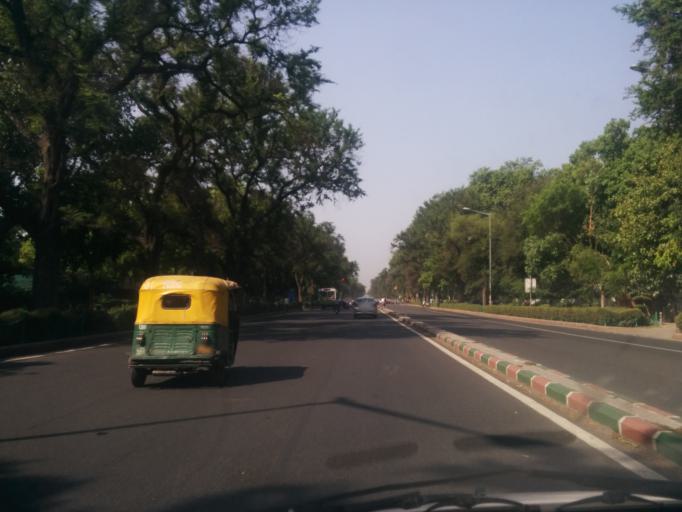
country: IN
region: NCT
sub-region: New Delhi
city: New Delhi
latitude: 28.6224
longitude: 77.2382
